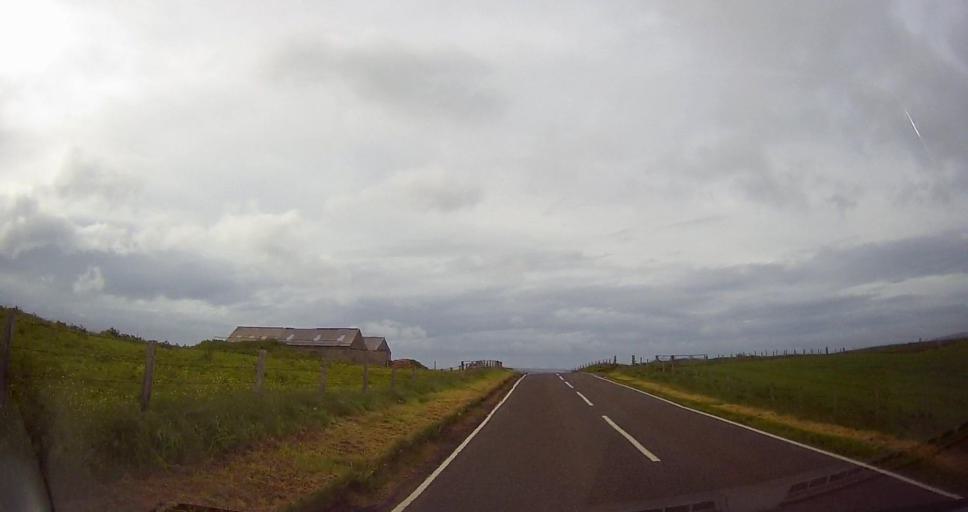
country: GB
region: Scotland
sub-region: Orkney Islands
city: Stromness
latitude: 58.9223
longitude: -3.1978
